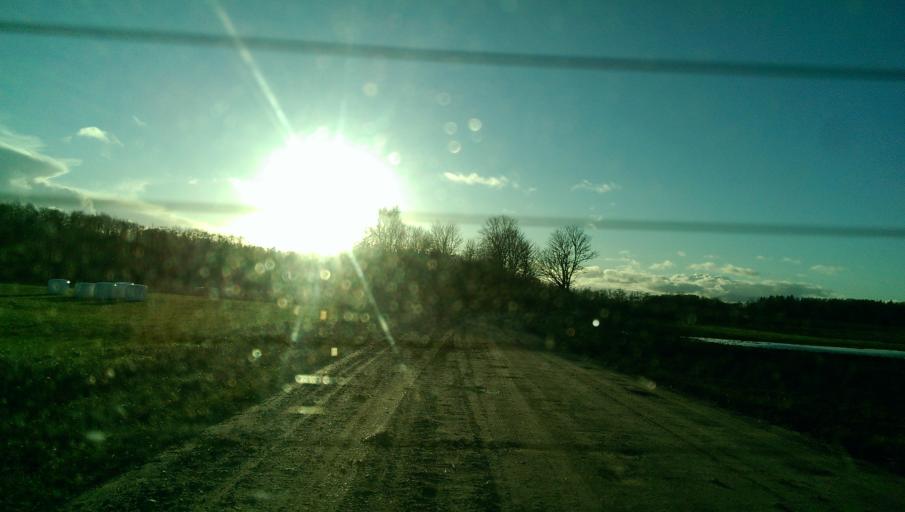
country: LV
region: Aizpute
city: Aizpute
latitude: 56.7519
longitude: 21.7711
